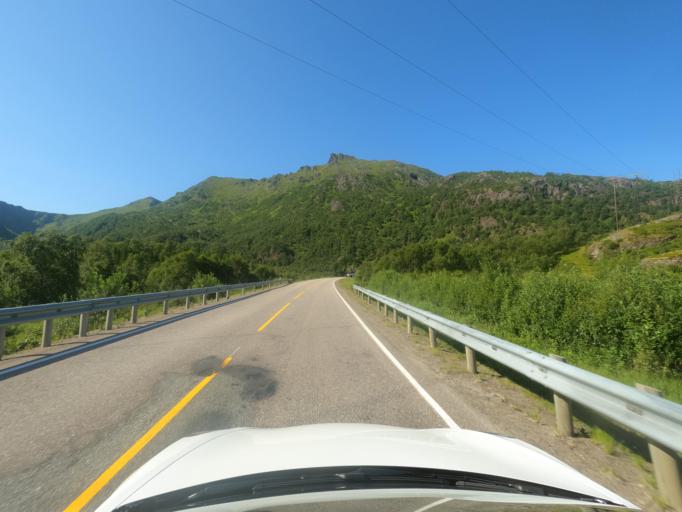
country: NO
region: Nordland
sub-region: Sortland
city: Sortland
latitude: 68.4613
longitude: 15.2587
